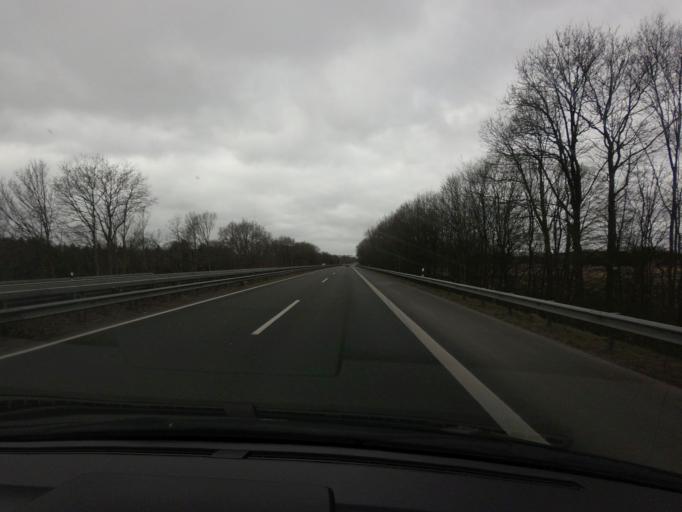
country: DE
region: Lower Saxony
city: Bad Zwischenahn
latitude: 53.2251
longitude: 8.0394
